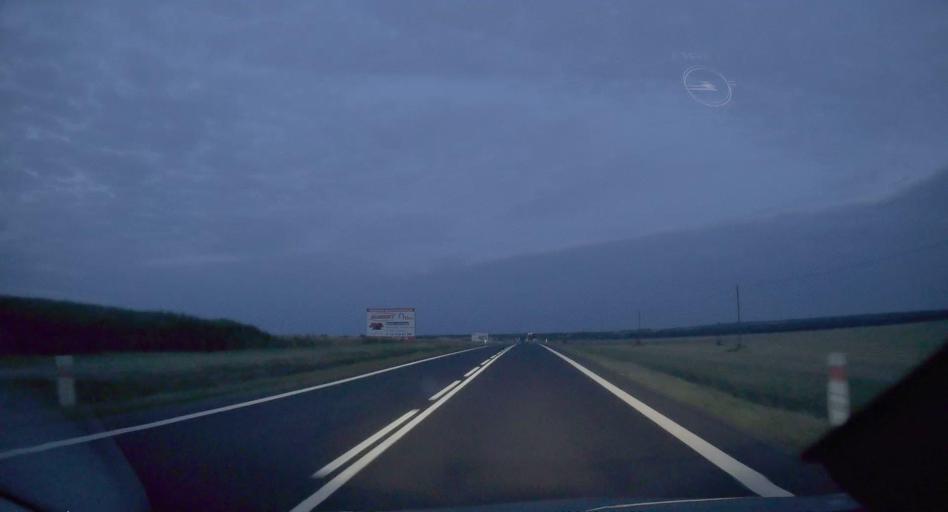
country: PL
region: Silesian Voivodeship
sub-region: Powiat klobucki
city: Klobuck
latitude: 50.8935
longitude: 18.9581
